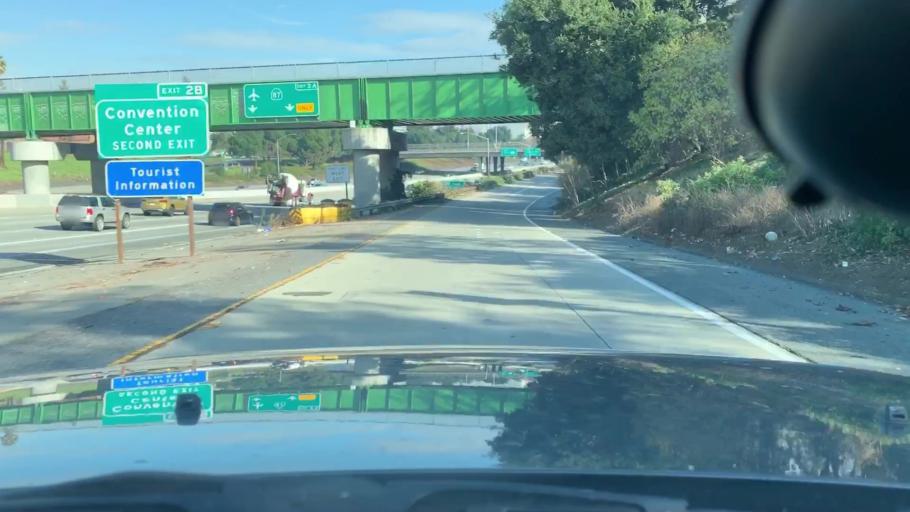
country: US
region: California
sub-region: Santa Clara County
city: Buena Vista
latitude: 37.3203
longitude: -121.9004
